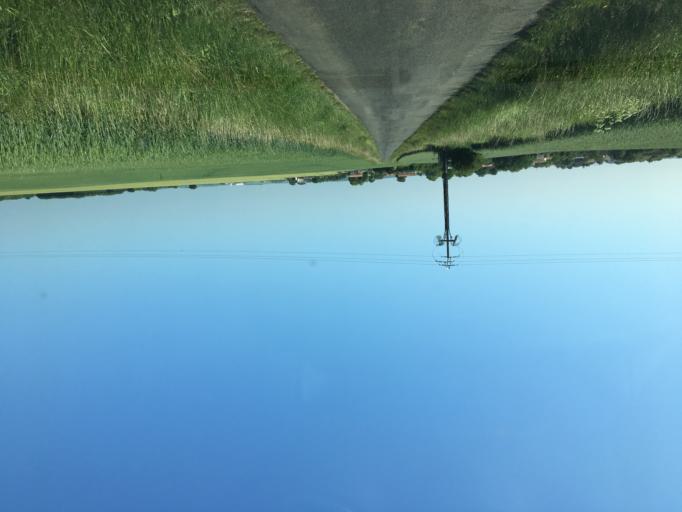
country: FR
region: Poitou-Charentes
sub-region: Departement des Deux-Sevres
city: Beauvoir-sur-Niort
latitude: 46.0810
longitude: -0.5079
